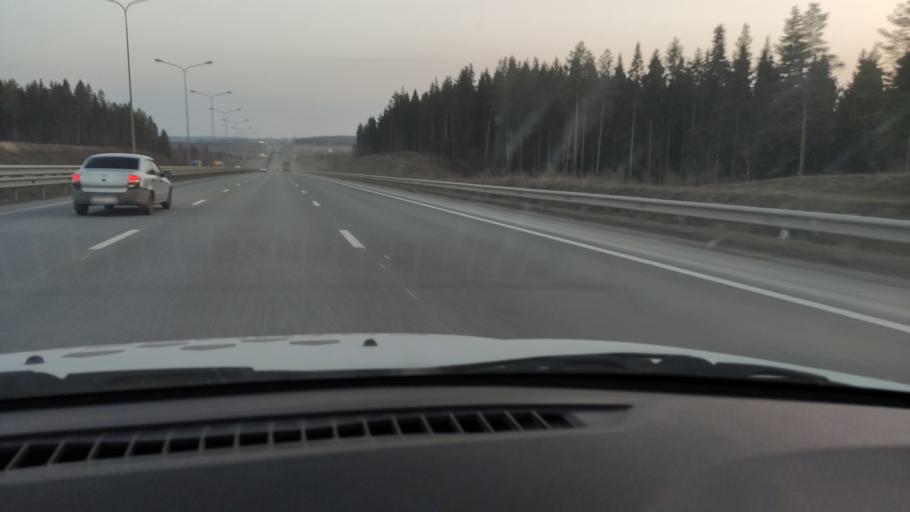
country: RU
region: Perm
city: Lobanovo
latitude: 57.8178
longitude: 56.3105
